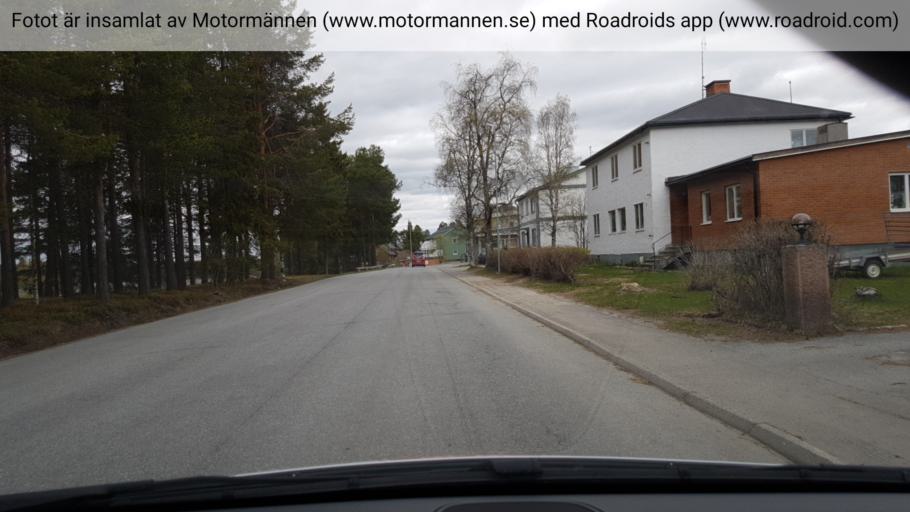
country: SE
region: Vaesterbotten
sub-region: Sorsele Kommun
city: Sorsele
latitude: 65.5331
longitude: 17.5381
